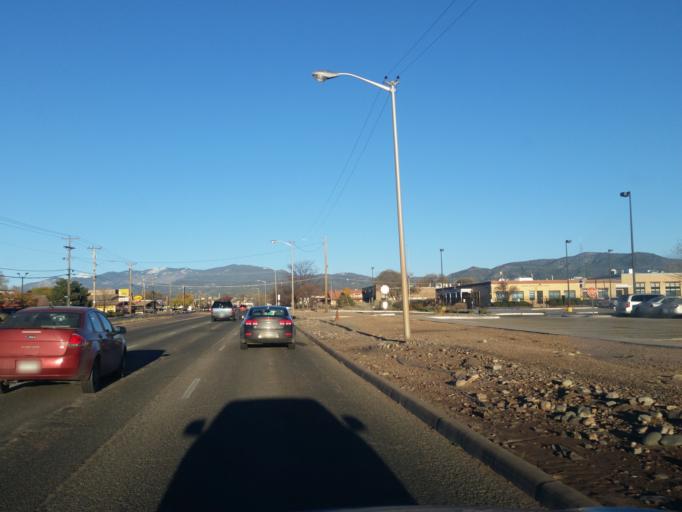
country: US
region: New Mexico
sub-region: Santa Fe County
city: Agua Fria
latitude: 35.6589
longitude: -105.9844
